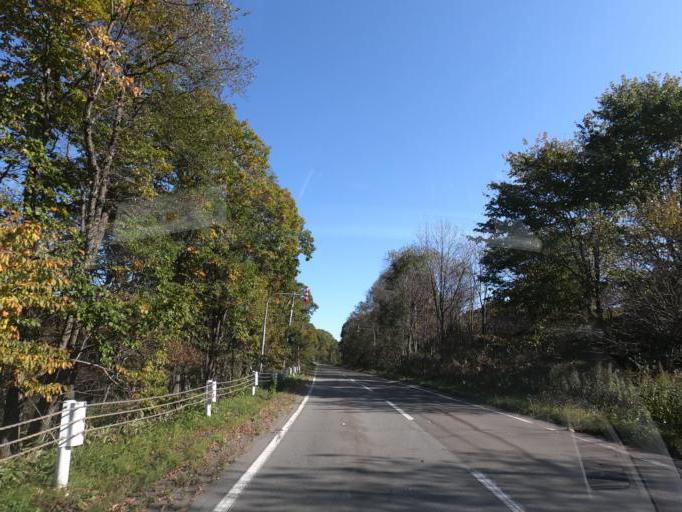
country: JP
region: Hokkaido
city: Obihiro
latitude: 42.6959
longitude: 143.4660
